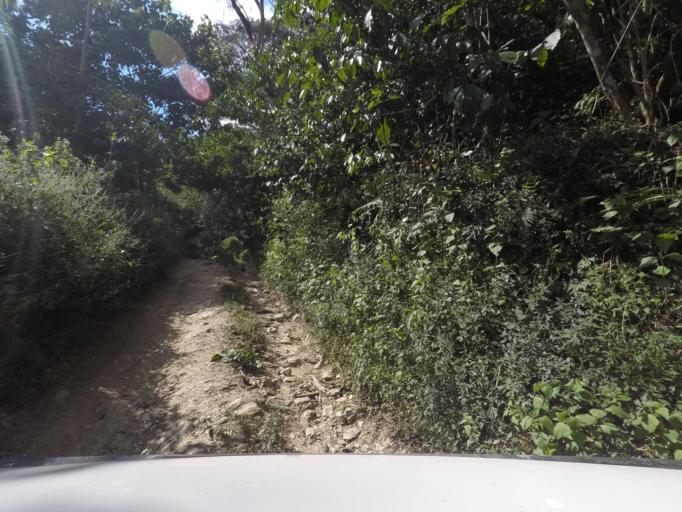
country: TL
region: Ermera
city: Gleno
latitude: -8.7205
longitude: 125.3099
